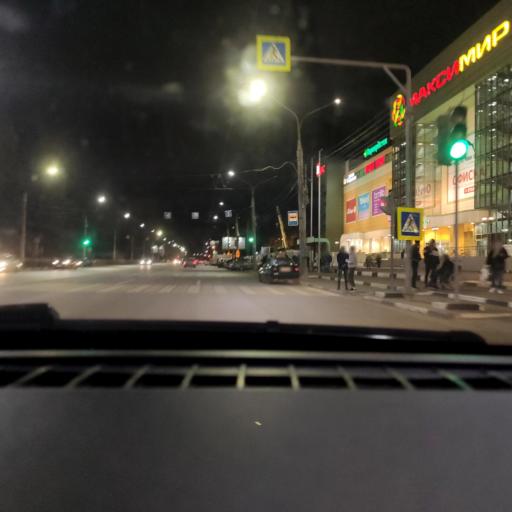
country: RU
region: Voronezj
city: Voronezh
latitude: 51.6970
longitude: 39.2717
